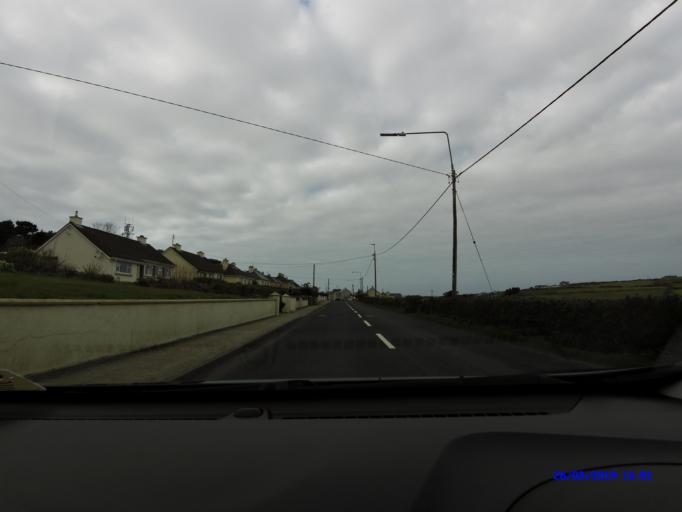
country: IE
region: Connaught
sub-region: Maigh Eo
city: Belmullet
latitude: 54.2212
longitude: -9.9800
